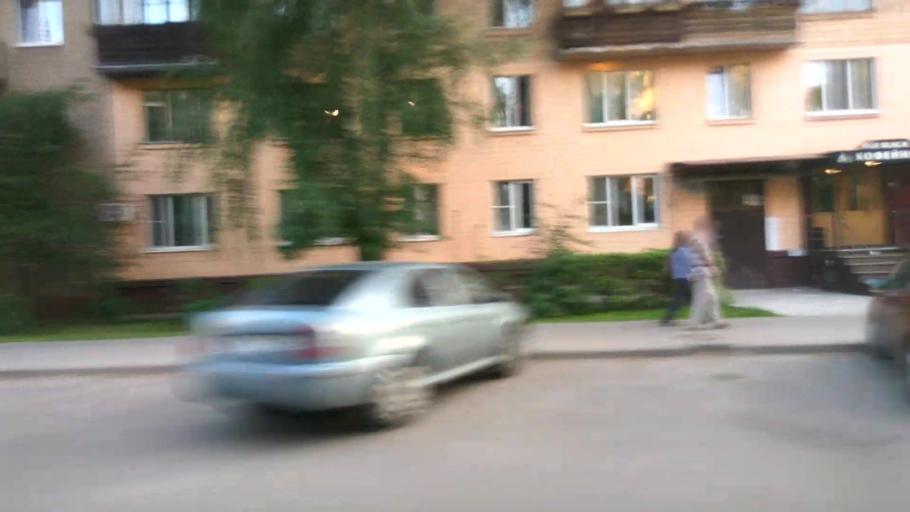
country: RU
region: Moskovskaya
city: Korolev
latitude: 55.9239
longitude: 37.8160
